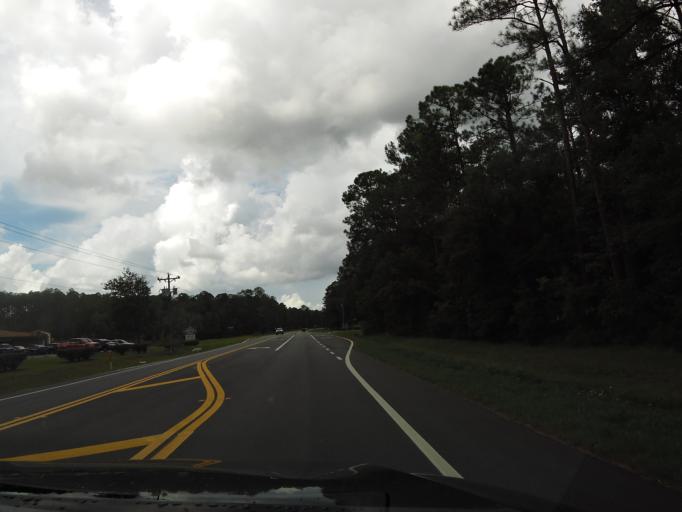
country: US
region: Florida
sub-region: Clay County
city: Middleburg
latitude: 30.0529
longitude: -81.8613
